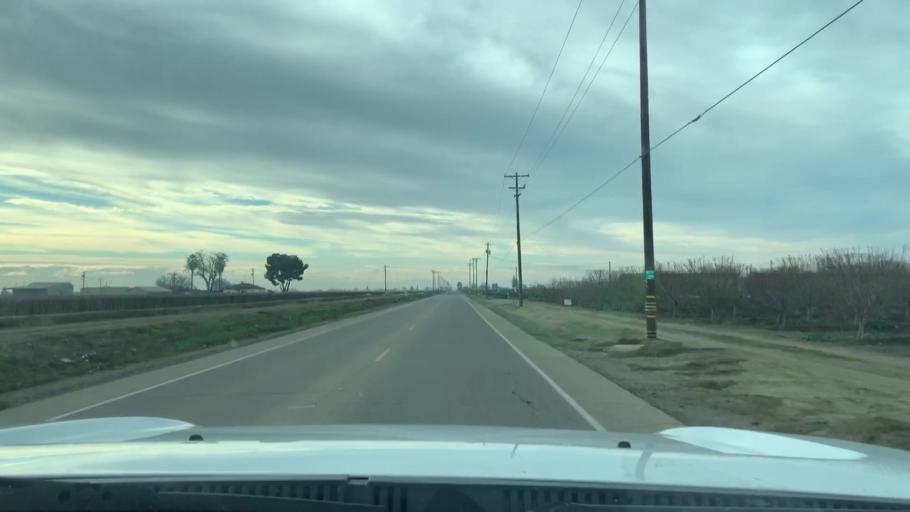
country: US
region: California
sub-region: Fresno County
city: Fowler
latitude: 36.6055
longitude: -119.7148
